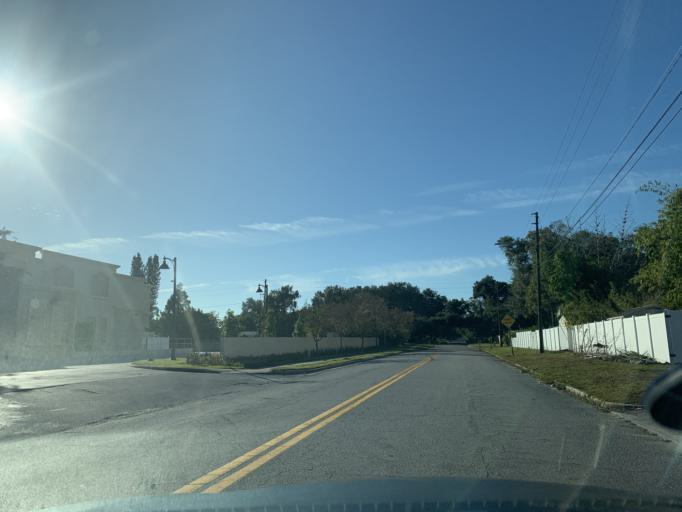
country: US
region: Florida
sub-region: Pinellas County
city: Bay Pines
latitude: 27.8053
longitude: -82.7497
